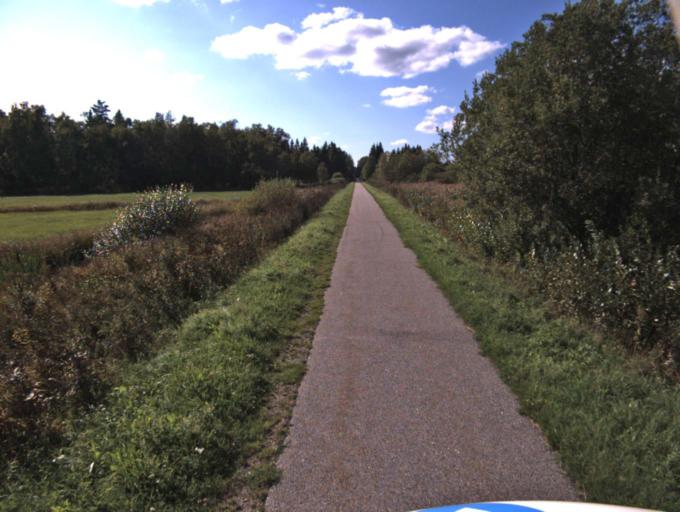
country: SE
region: Vaestra Goetaland
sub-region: Ulricehamns Kommun
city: Ulricehamn
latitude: 57.8361
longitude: 13.2546
